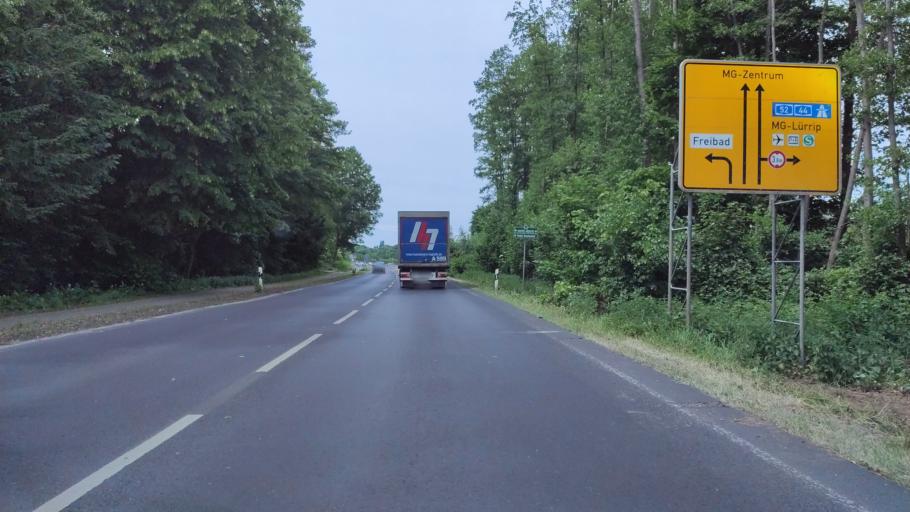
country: DE
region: North Rhine-Westphalia
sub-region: Regierungsbezirk Dusseldorf
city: Monchengladbach
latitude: 51.1976
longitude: 6.4760
